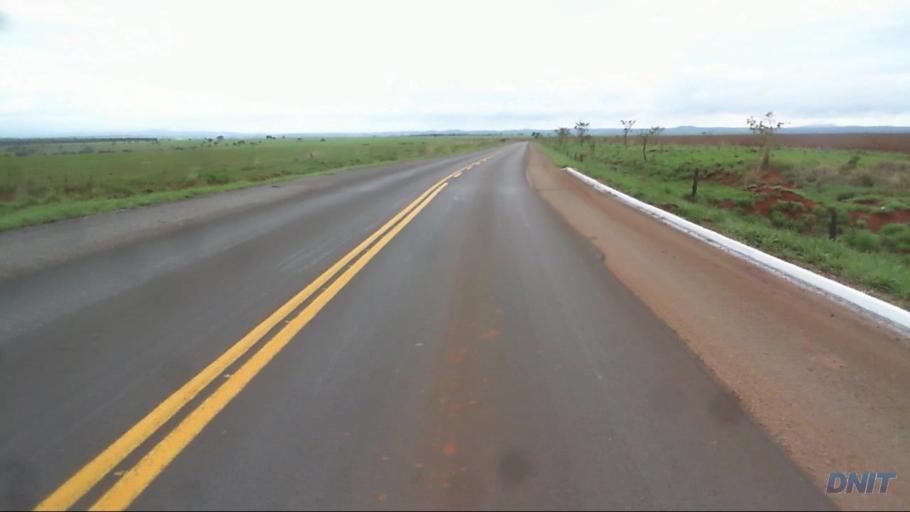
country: BR
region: Goias
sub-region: Padre Bernardo
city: Padre Bernardo
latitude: -15.1731
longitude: -48.3902
